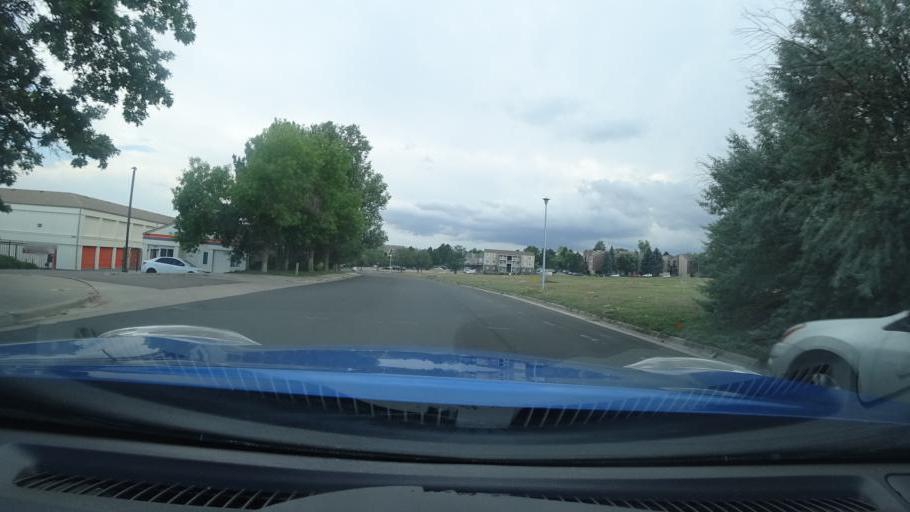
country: US
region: Colorado
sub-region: Adams County
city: Aurora
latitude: 39.6960
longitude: -104.8072
